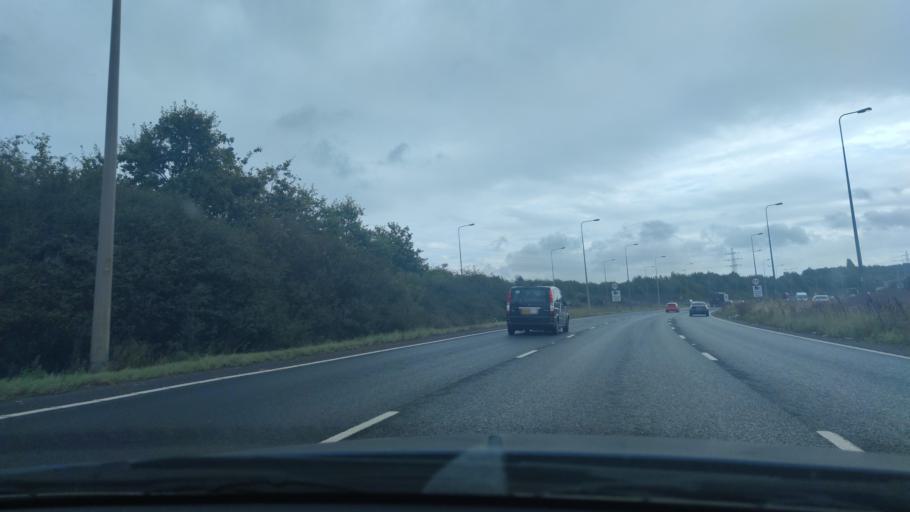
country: GB
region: England
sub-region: Essex
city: Purfleet
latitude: 51.5000
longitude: 0.2304
